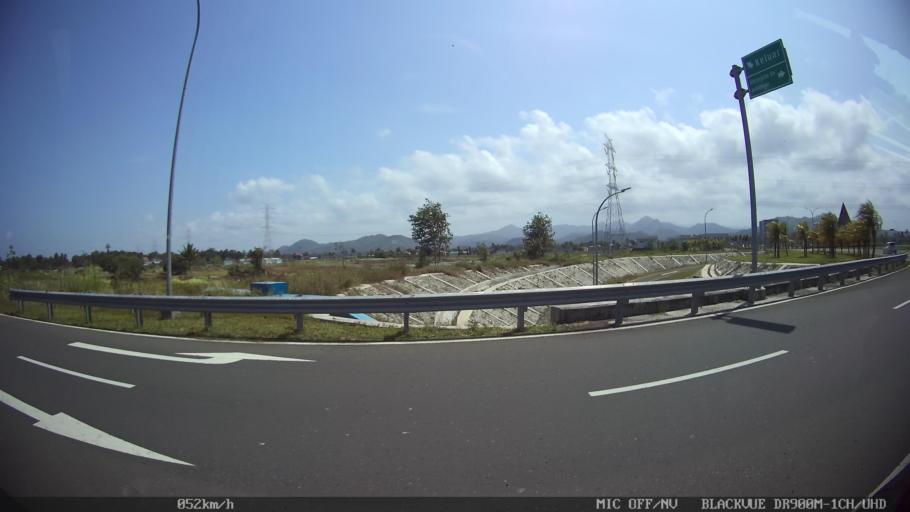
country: ID
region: Daerah Istimewa Yogyakarta
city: Srandakan
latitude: -7.8916
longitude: 110.0610
